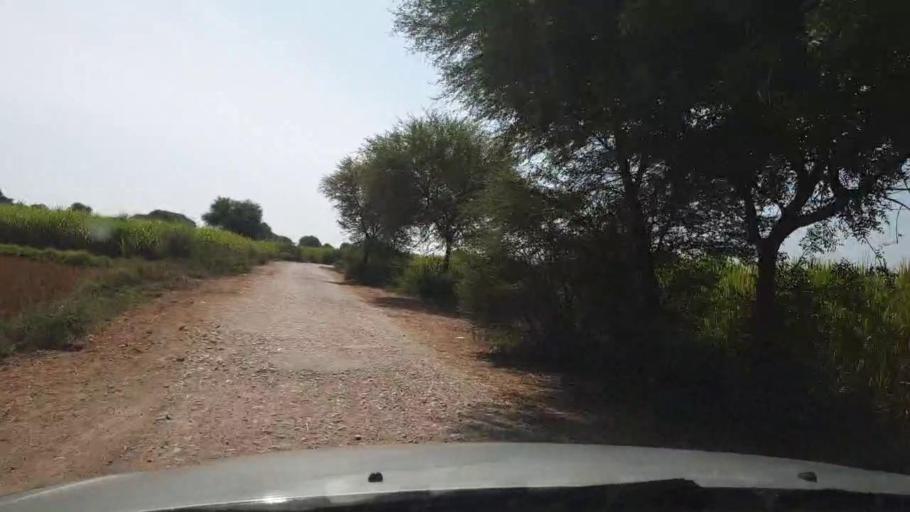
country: PK
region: Sindh
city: Bulri
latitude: 25.0280
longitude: 68.3014
